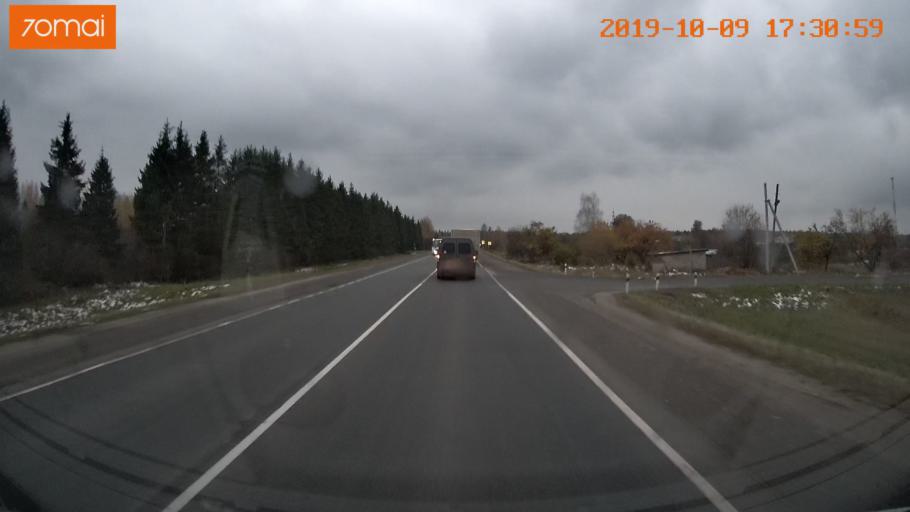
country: RU
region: Ivanovo
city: Bogorodskoye
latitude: 57.1386
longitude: 41.0436
